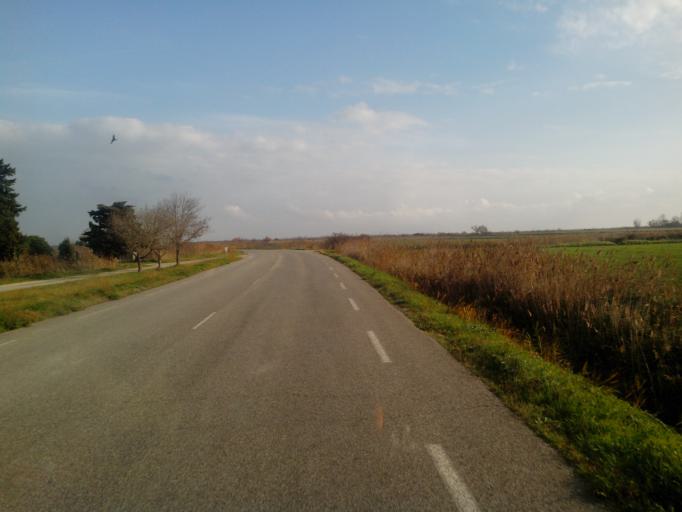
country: FR
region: Languedoc-Roussillon
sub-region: Departement du Gard
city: Saint-Gilles
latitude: 43.6060
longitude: 4.4817
